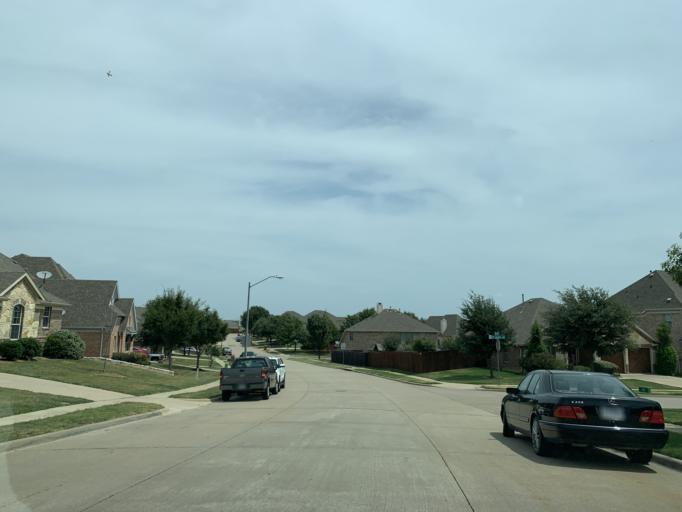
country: US
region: Texas
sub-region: Dallas County
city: Cedar Hill
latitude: 32.6510
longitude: -97.0006
